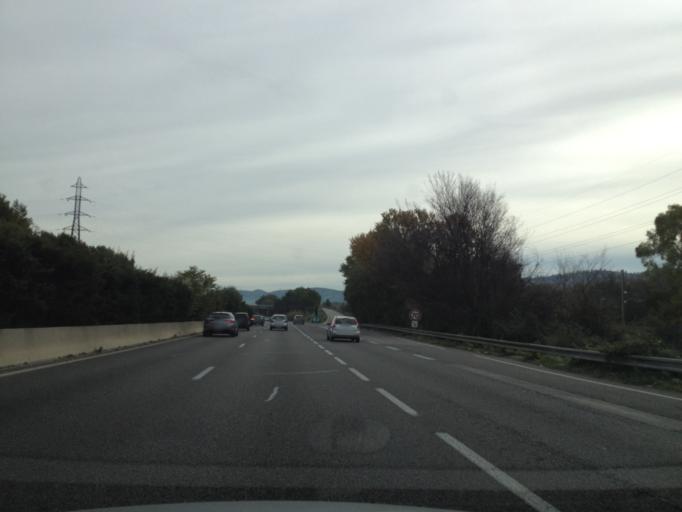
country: FR
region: Provence-Alpes-Cote d'Azur
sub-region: Departement des Bouches-du-Rhone
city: La Penne-sur-Huveaune
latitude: 43.2862
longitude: 5.5097
